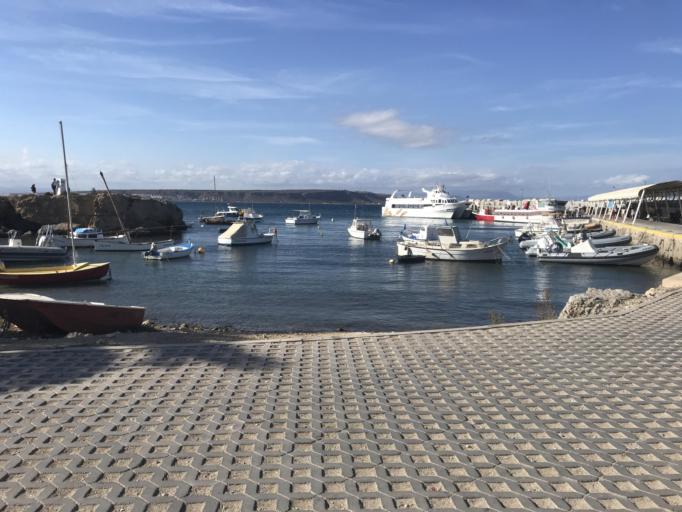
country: ES
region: Valencia
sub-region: Provincia de Alicante
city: Santa Pola
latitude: 38.1652
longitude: -0.4776
